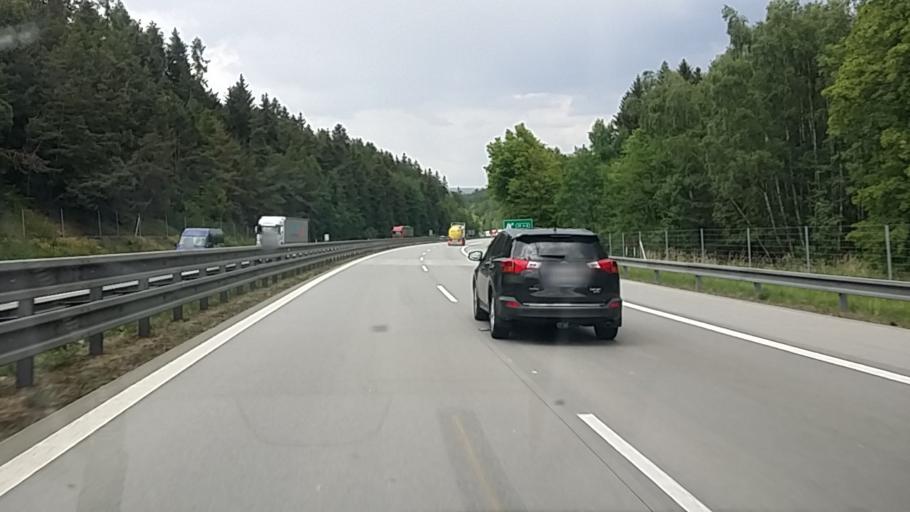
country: CZ
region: Central Bohemia
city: Ondrejov
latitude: 49.8484
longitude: 14.7972
